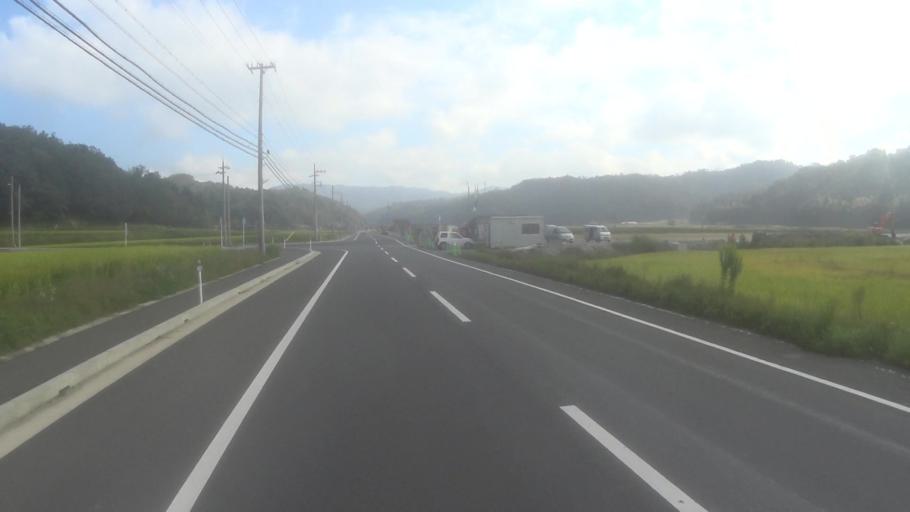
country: JP
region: Kyoto
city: Miyazu
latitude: 35.5770
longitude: 135.1209
